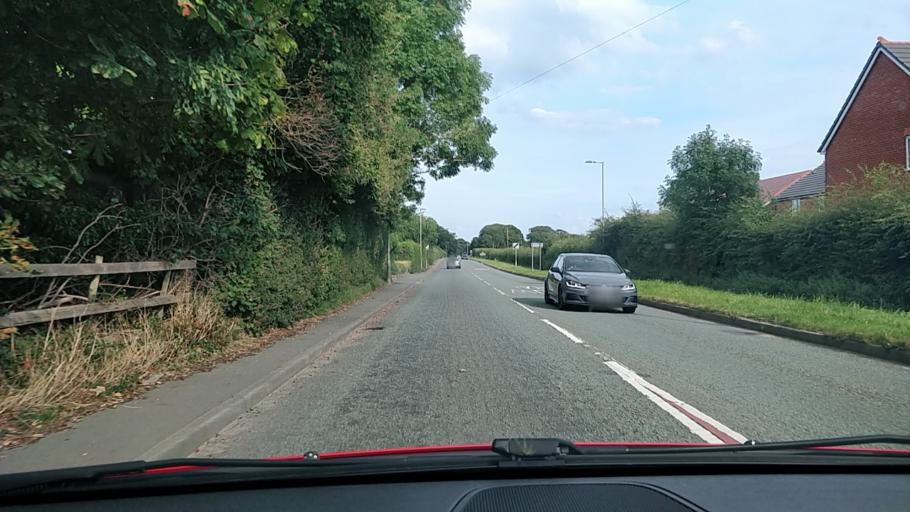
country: GB
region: Wales
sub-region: County of Flintshire
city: Penyffordd
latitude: 53.1570
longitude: -3.0374
